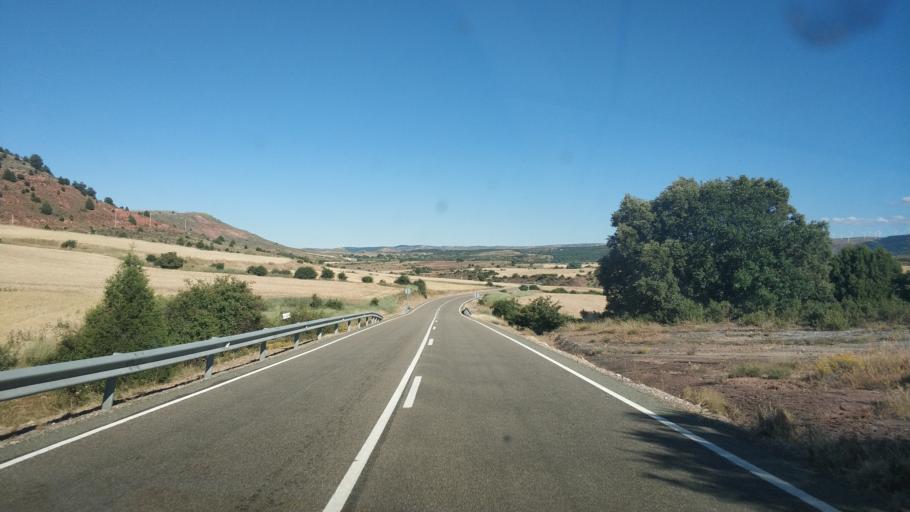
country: ES
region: Castille and Leon
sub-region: Provincia de Soria
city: Montejo de Tiermes
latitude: 41.3503
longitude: -3.1635
